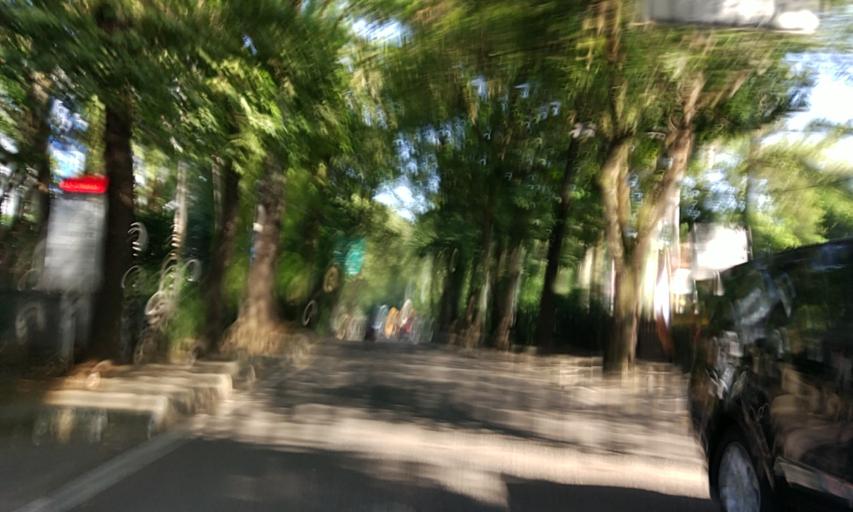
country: ID
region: West Java
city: Bandung
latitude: -6.8874
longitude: 107.6129
